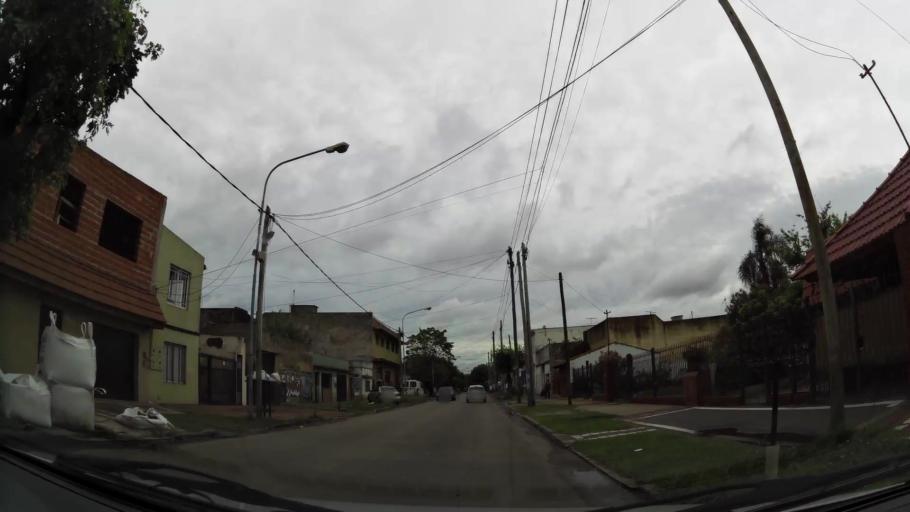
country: AR
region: Buenos Aires
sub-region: Partido de Lanus
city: Lanus
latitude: -34.7201
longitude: -58.3789
